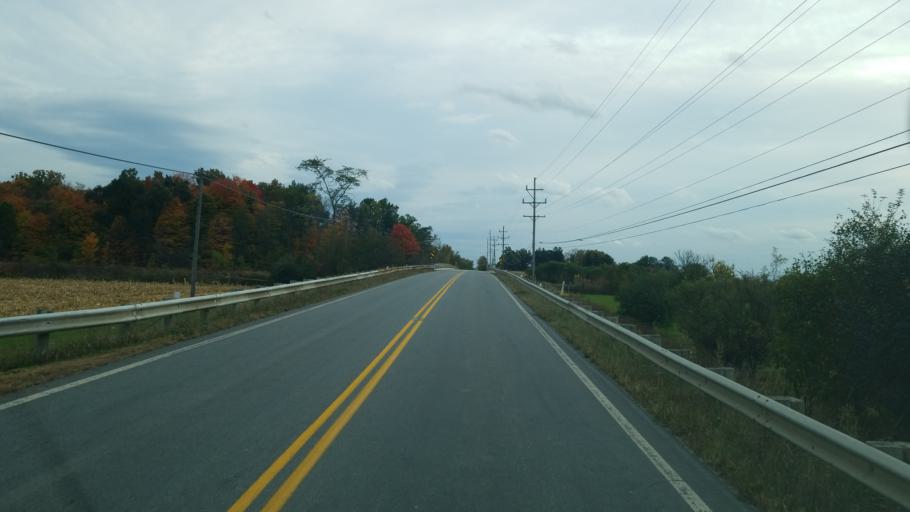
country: US
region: Ohio
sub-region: Ashland County
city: Ashland
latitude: 40.8383
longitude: -82.2987
